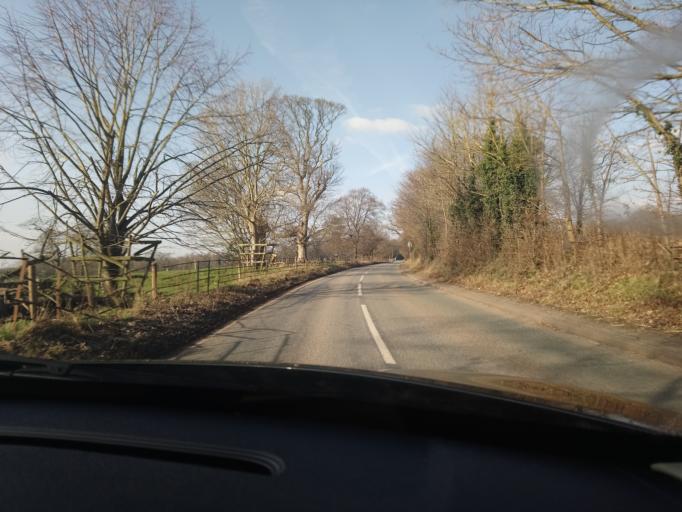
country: GB
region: England
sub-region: Shropshire
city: Shrewsbury
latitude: 52.7309
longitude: -2.7752
